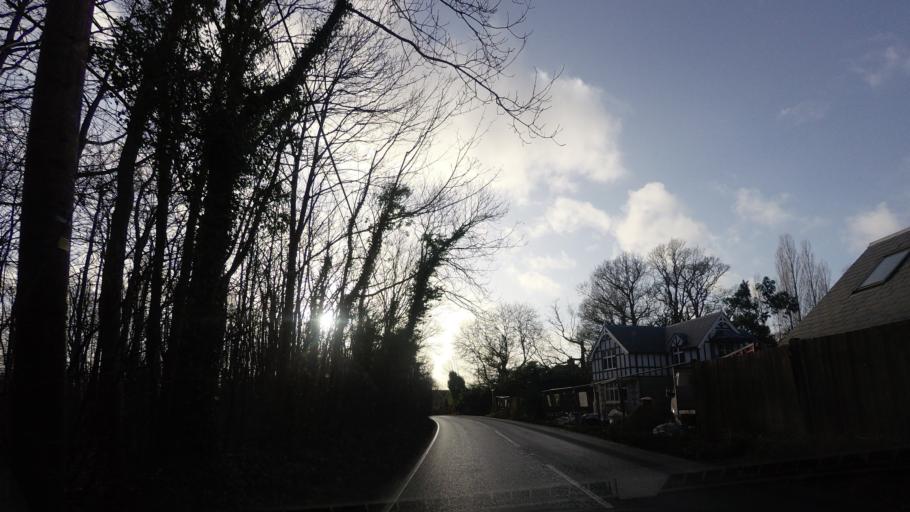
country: GB
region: England
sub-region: Kent
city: Tonbridge
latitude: 51.2280
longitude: 0.2923
